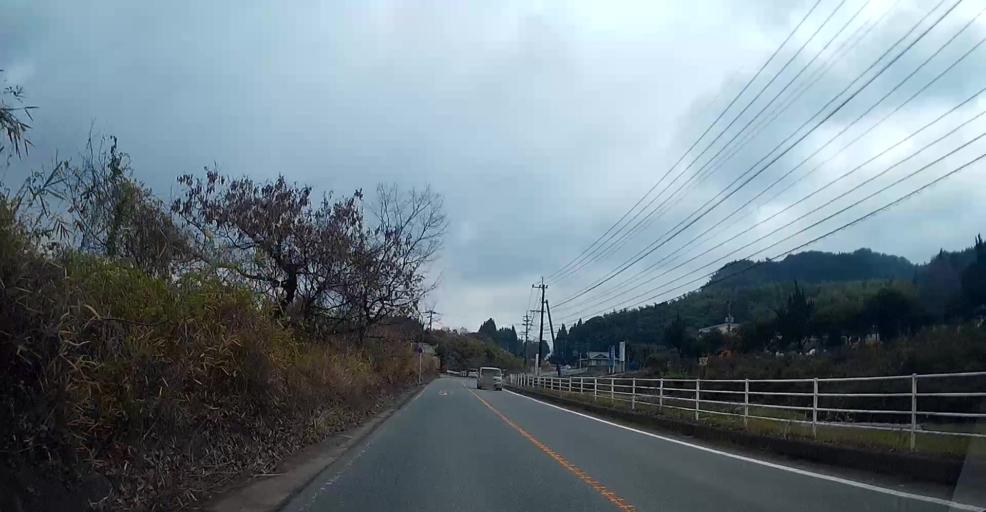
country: JP
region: Kumamoto
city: Matsubase
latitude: 32.6464
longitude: 130.7272
